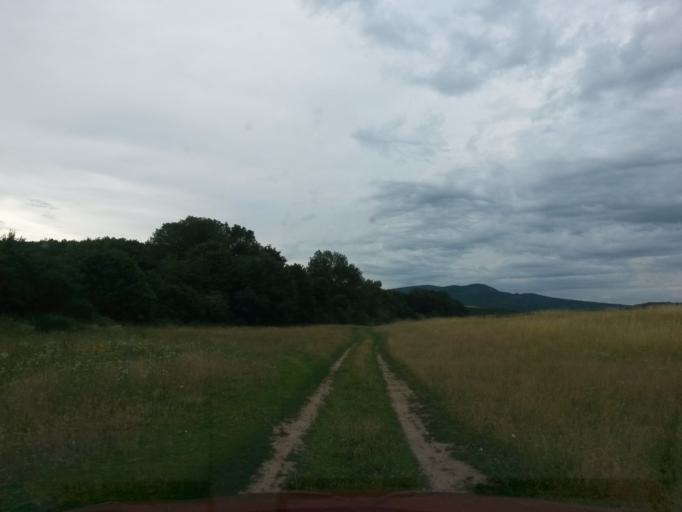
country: SK
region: Banskobystricky
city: Velky Krtis
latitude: 48.3108
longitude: 19.4161
